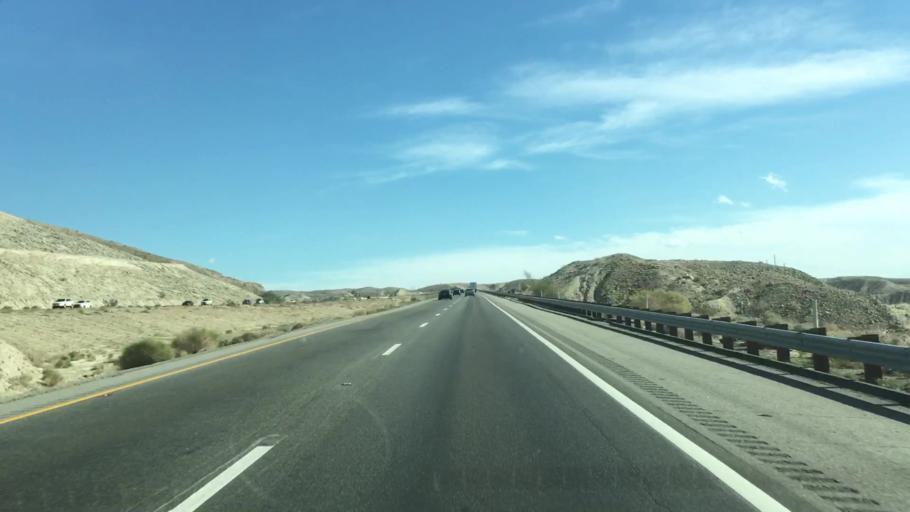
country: US
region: California
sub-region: Riverside County
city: Coachella
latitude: 33.7004
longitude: -116.1115
